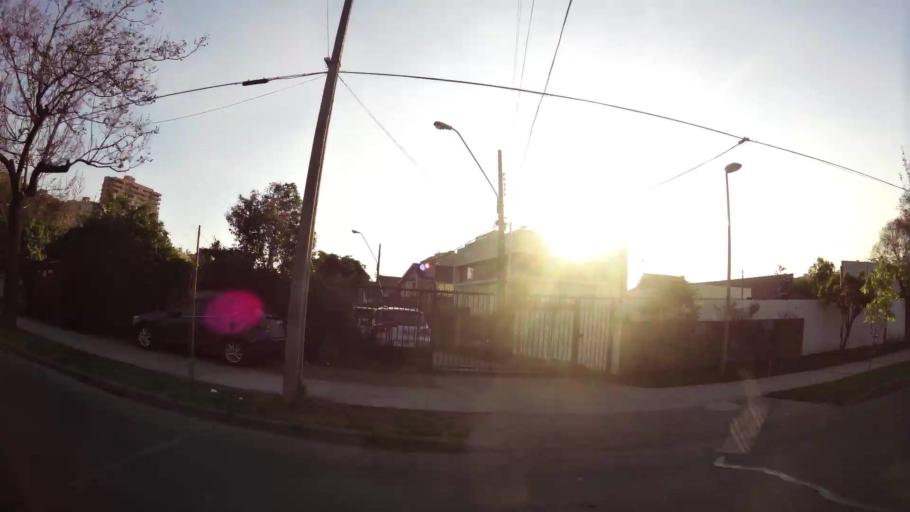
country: CL
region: Santiago Metropolitan
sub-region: Provincia de Santiago
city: Villa Presidente Frei, Nunoa, Santiago, Chile
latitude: -33.4008
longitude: -70.5599
